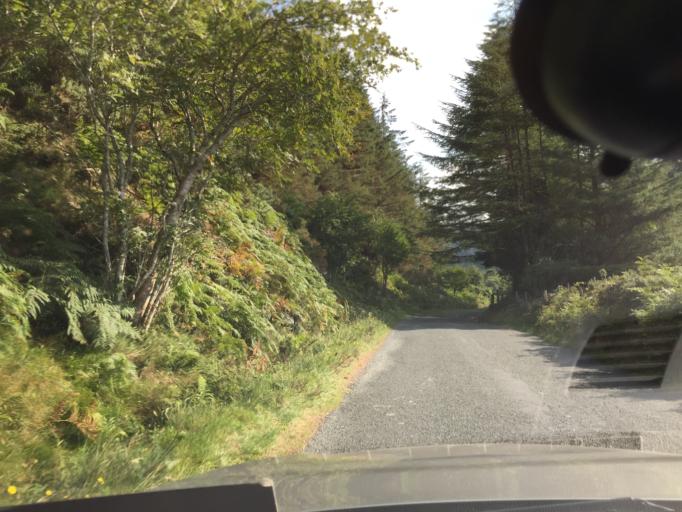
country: IE
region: Leinster
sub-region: Wicklow
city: Rathdrum
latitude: 53.0565
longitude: -6.3311
